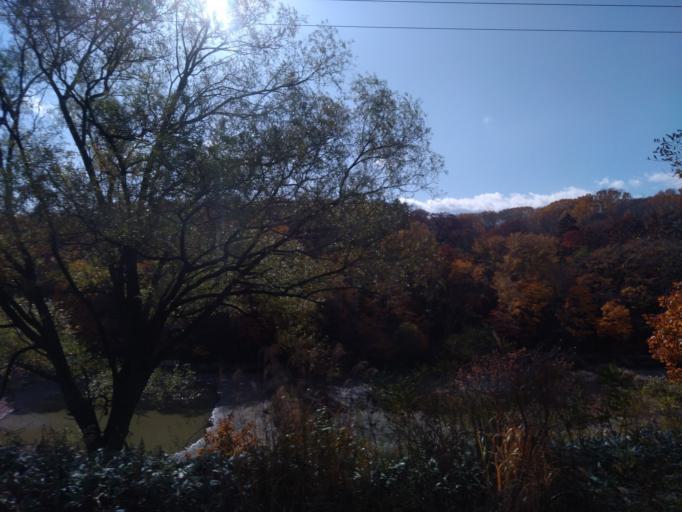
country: JP
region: Hokkaido
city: Kitahiroshima
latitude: 43.0023
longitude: 141.5109
